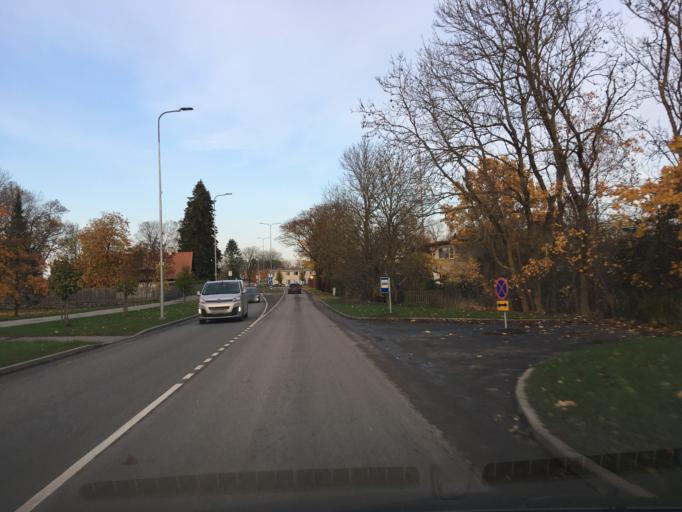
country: EE
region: Harju
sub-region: Harku vald
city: Tabasalu
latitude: 59.4262
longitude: 24.5447
